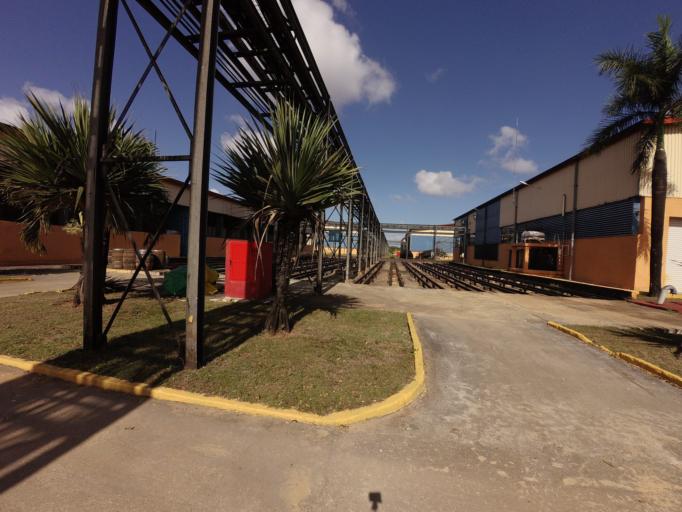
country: CU
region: Mayabeque
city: San Jose de las Lajas
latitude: 22.9311
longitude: -82.1022
